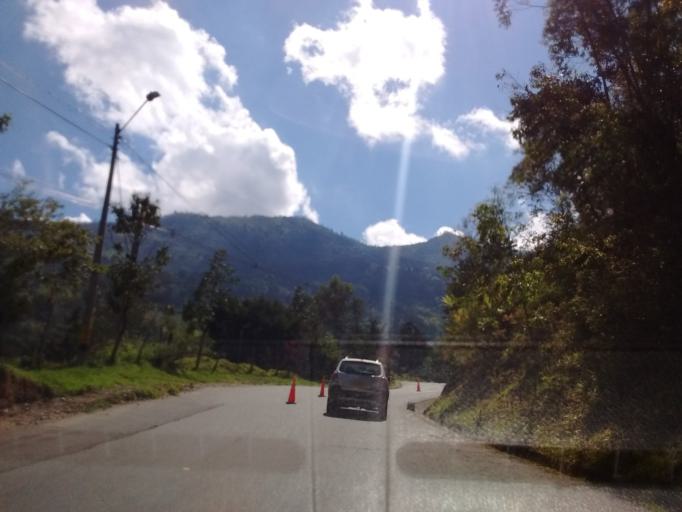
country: CO
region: Antioquia
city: Medellin
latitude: 6.2272
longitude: -75.5217
